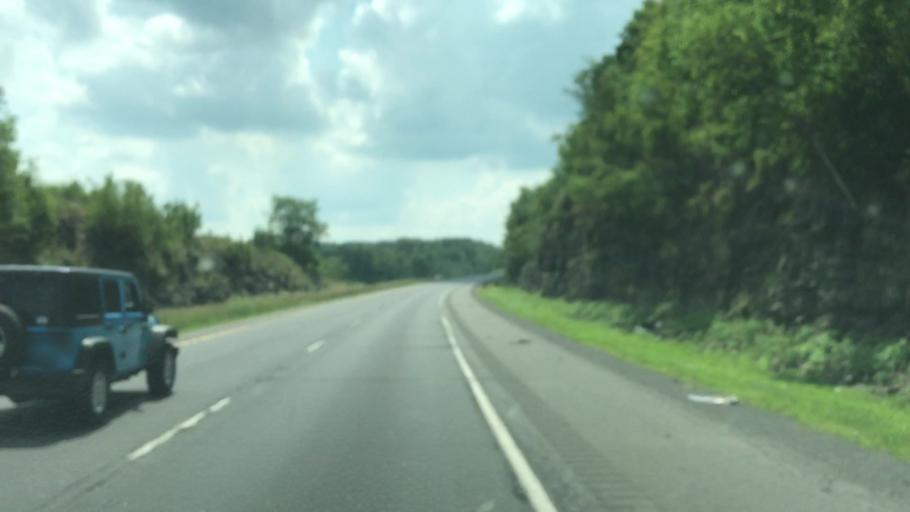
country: US
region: Pennsylvania
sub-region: Lackawanna County
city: Mount Cobb
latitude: 41.3882
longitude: -75.4623
